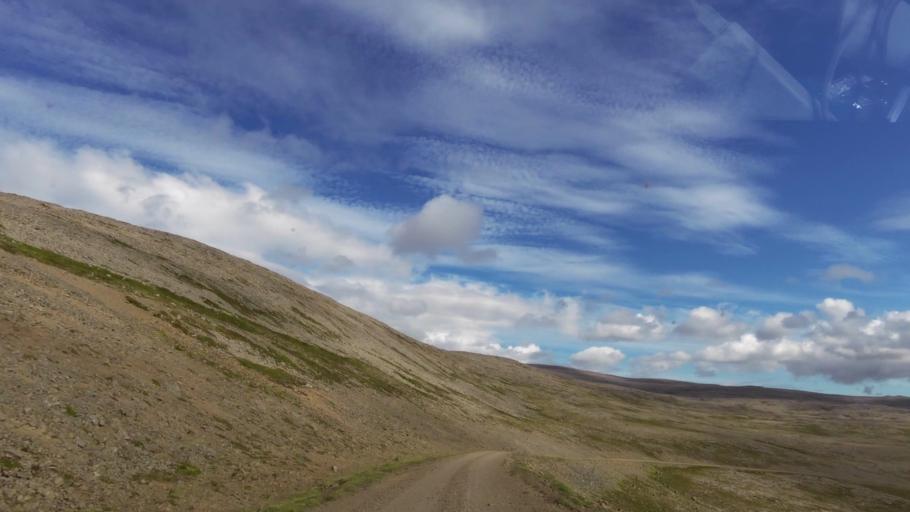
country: IS
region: West
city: Olafsvik
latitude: 65.6174
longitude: -24.3086
